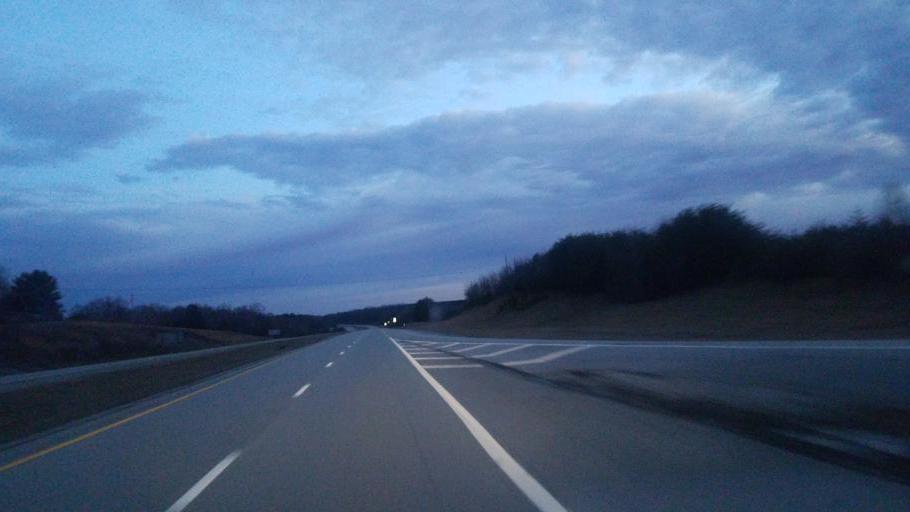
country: US
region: Tennessee
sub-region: Van Buren County
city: Spencer
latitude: 35.6315
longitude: -85.4754
